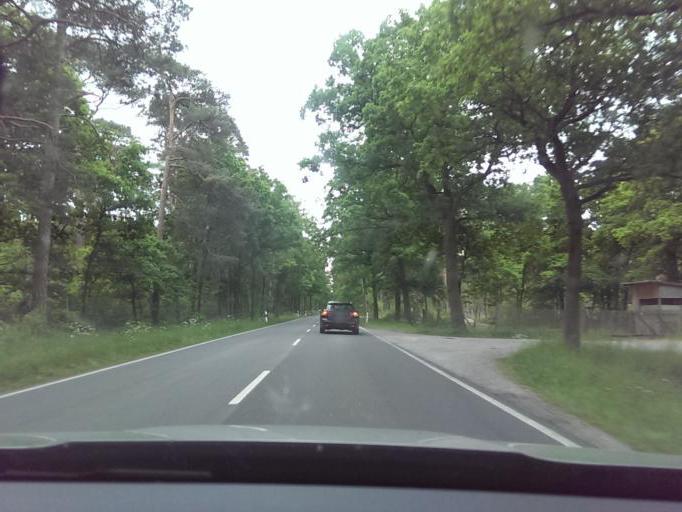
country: DE
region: Lower Saxony
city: Essel
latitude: 52.6545
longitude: 9.6725
